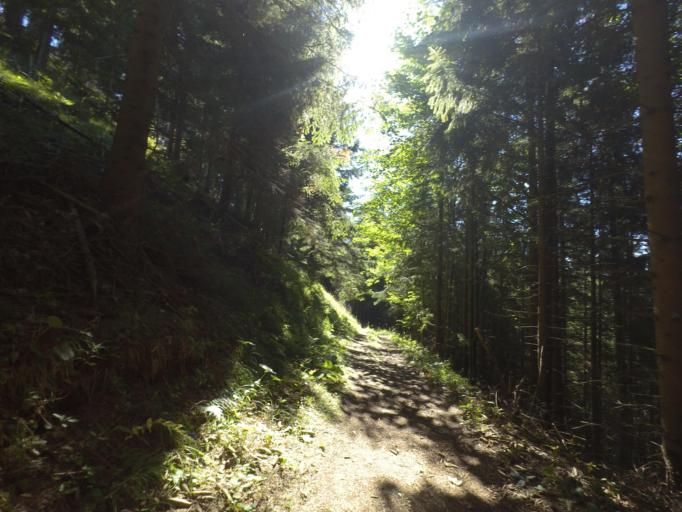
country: AT
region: Styria
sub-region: Politischer Bezirk Weiz
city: Passail
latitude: 47.3323
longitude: 15.4636
